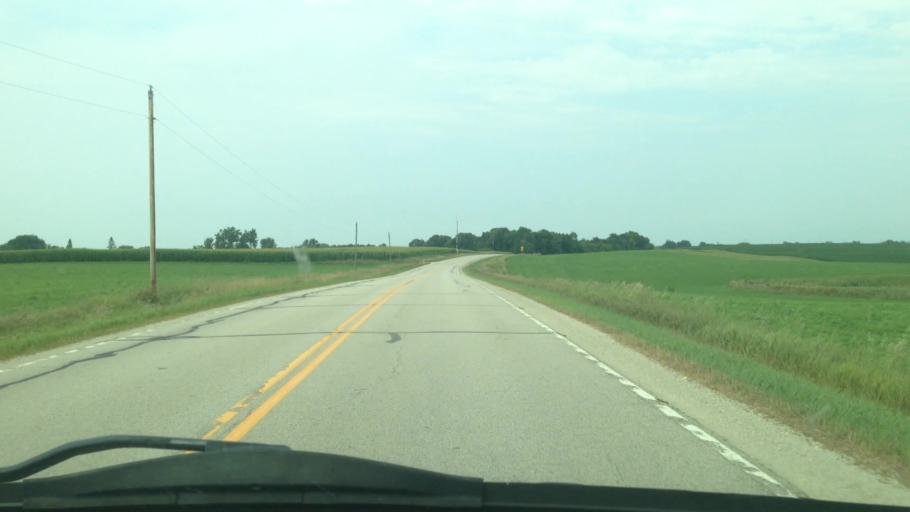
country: US
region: Minnesota
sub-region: Fillmore County
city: Preston
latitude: 43.7617
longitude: -91.9628
